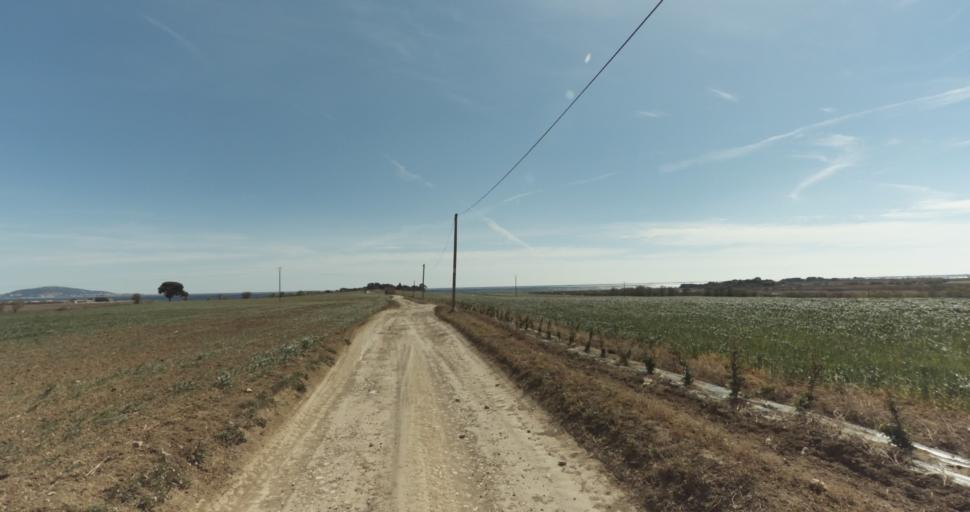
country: FR
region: Languedoc-Roussillon
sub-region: Departement de l'Herault
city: Pinet
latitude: 43.4040
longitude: 3.5535
